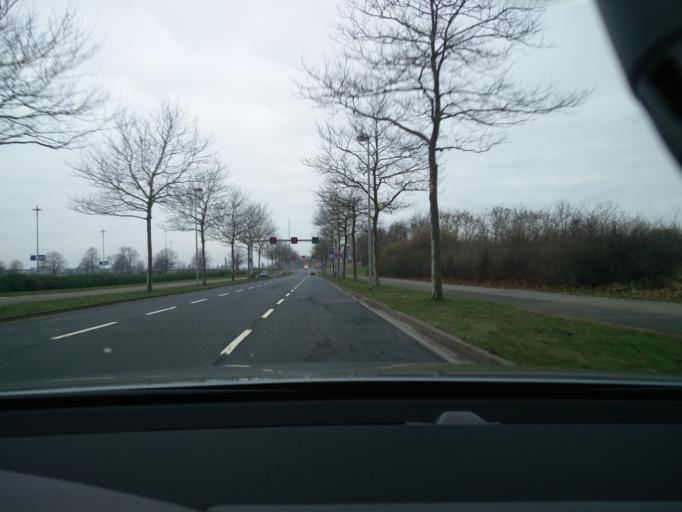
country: DE
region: Lower Saxony
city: Laatzen
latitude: 52.3307
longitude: 9.8231
